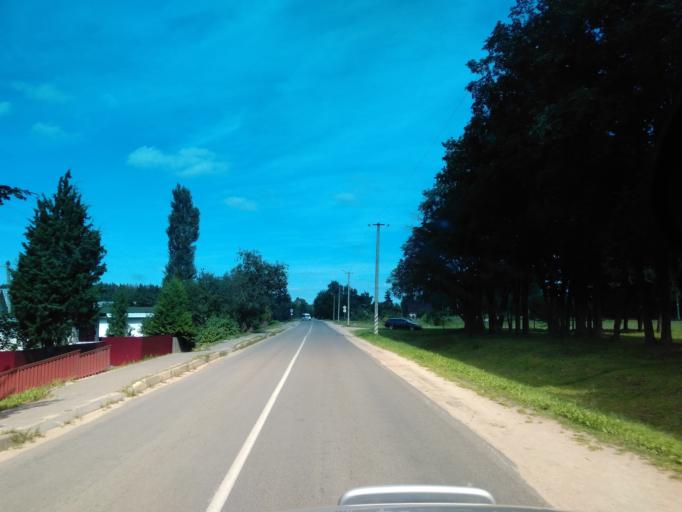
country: BY
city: Fanipol
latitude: 53.7466
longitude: 27.3388
